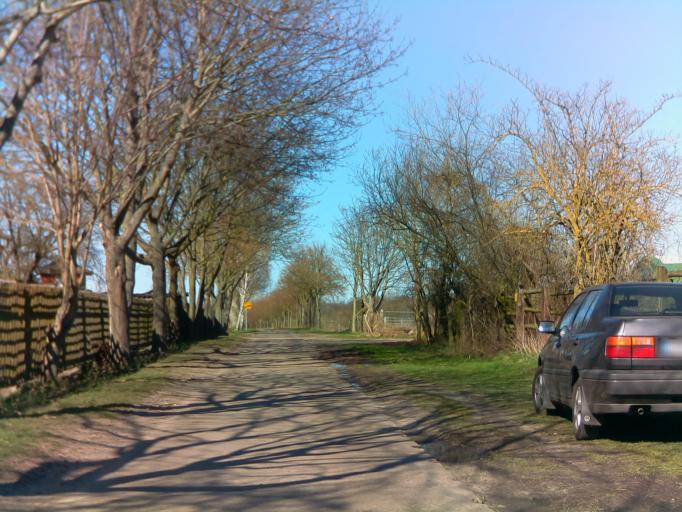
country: DE
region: Brandenburg
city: Werder
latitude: 52.4343
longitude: 12.9549
